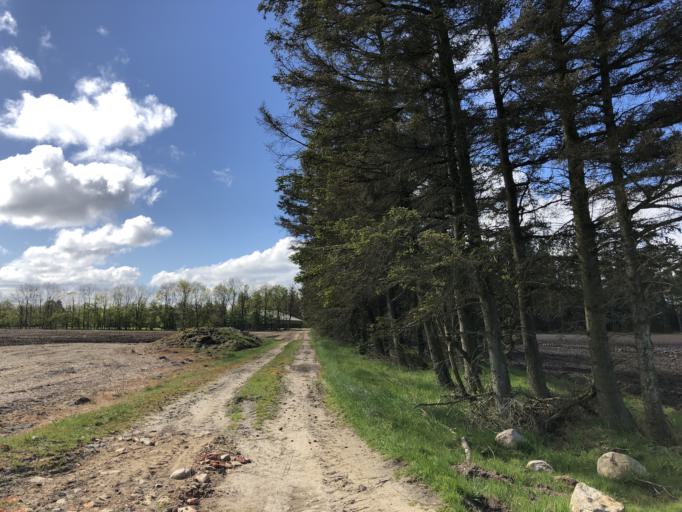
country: DK
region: Central Jutland
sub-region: Holstebro Kommune
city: Ulfborg
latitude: 56.2404
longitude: 8.4682
